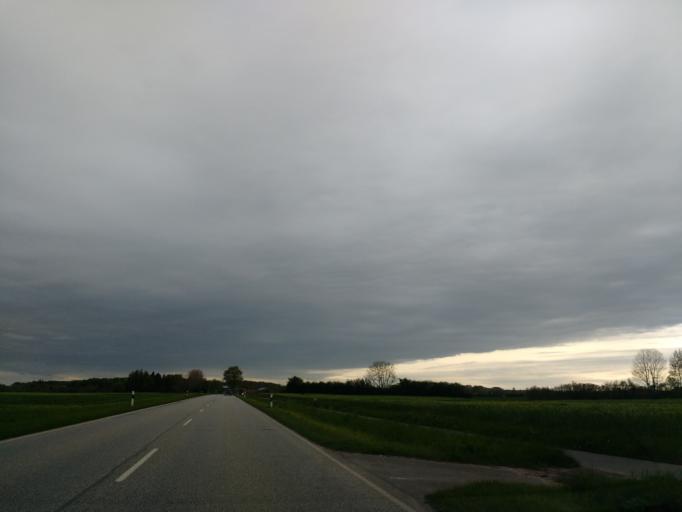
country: DE
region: Schleswig-Holstein
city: Rabel
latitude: 54.6831
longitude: 9.9388
